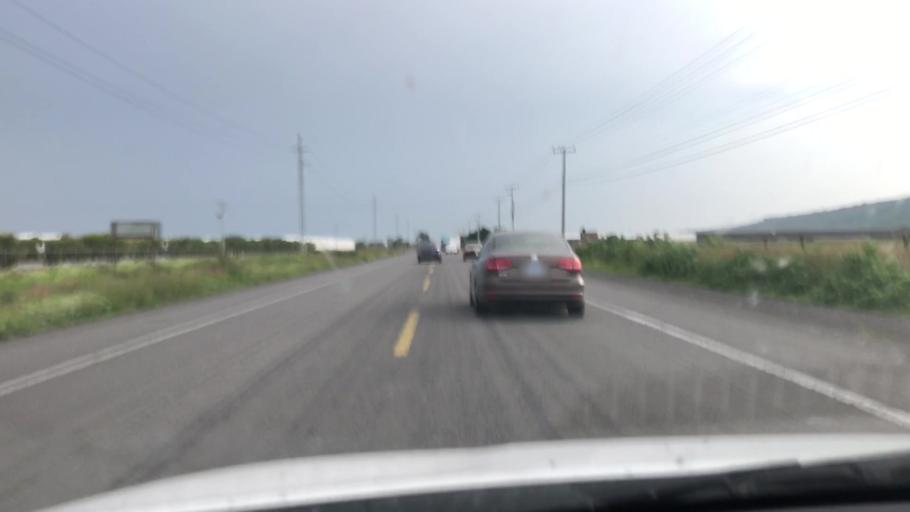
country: MX
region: Michoacan
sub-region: Vista Hermosa
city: Los Pilares
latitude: 20.2779
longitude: -102.3784
